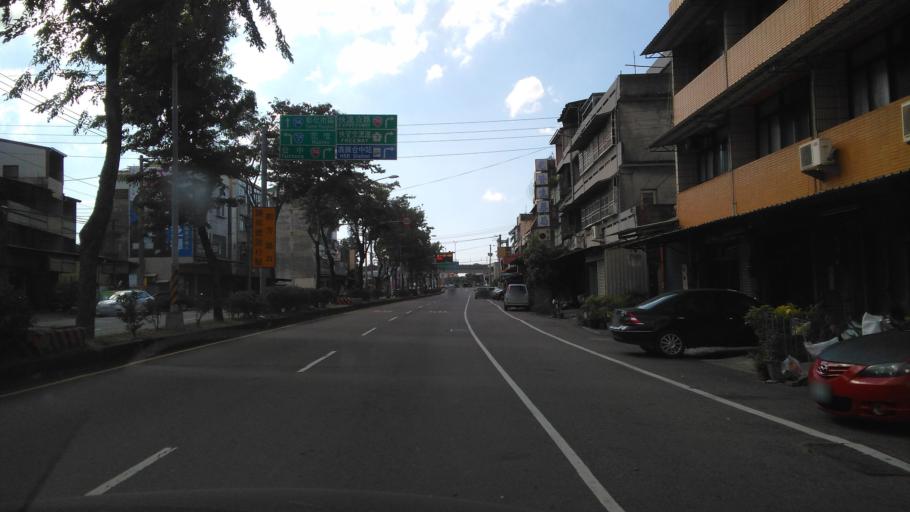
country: TW
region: Taiwan
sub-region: Changhua
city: Chang-hua
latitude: 24.0820
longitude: 120.5972
